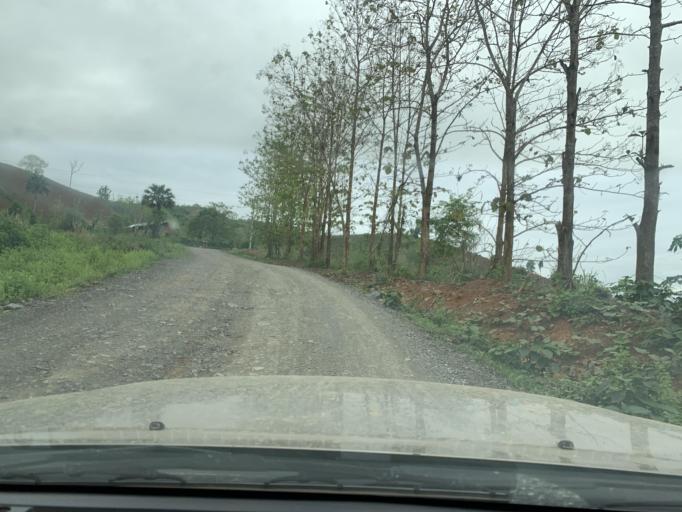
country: TH
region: Nan
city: Mae Charim
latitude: 18.4186
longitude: 101.4636
